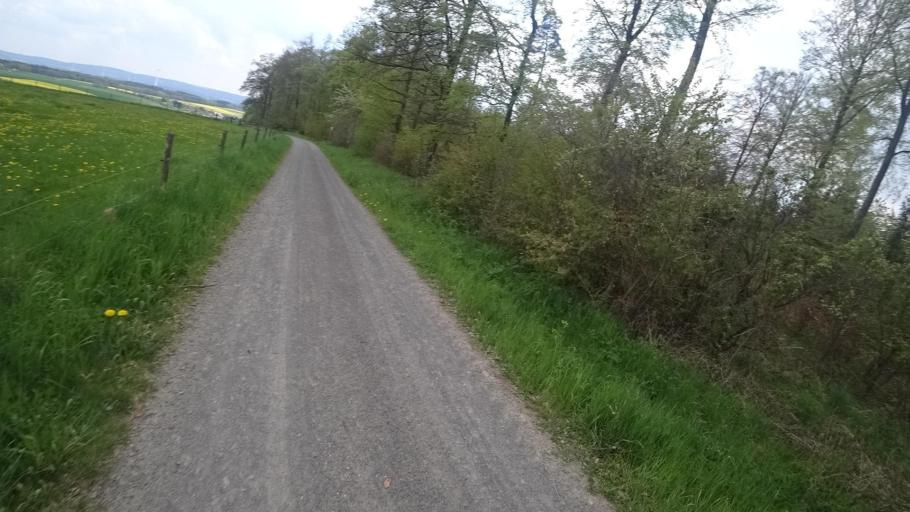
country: DE
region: Rheinland-Pfalz
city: Klosterkumbd
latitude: 50.0377
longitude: 7.5278
